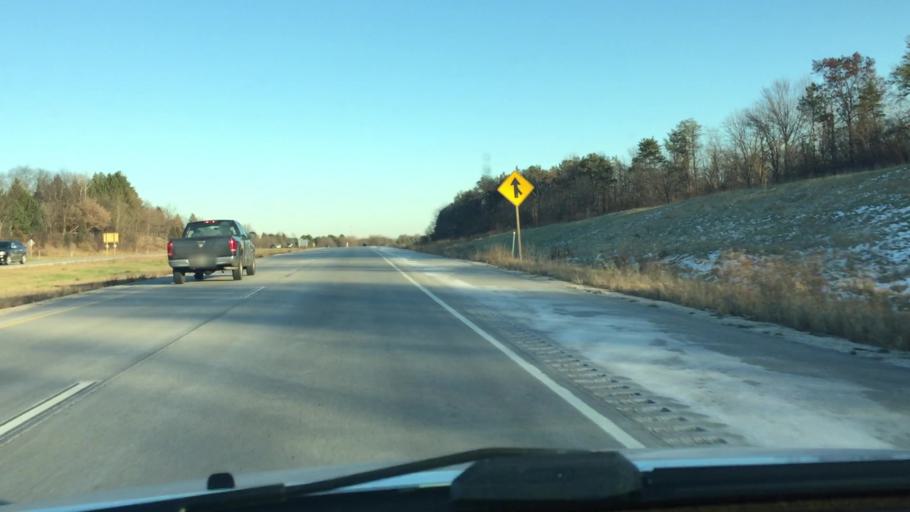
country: US
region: Wisconsin
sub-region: Waukesha County
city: Hartland
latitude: 43.1095
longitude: -88.3324
